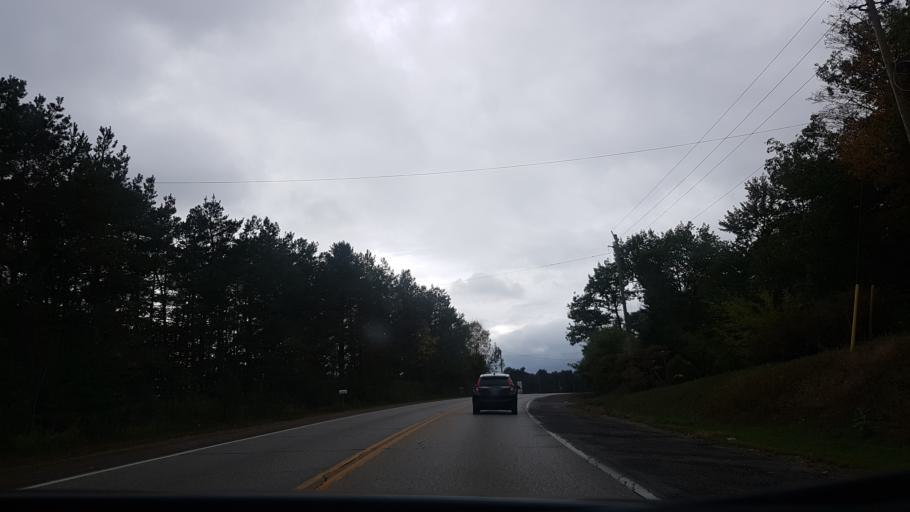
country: CA
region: Ontario
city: Uxbridge
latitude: 44.1037
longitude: -79.0978
